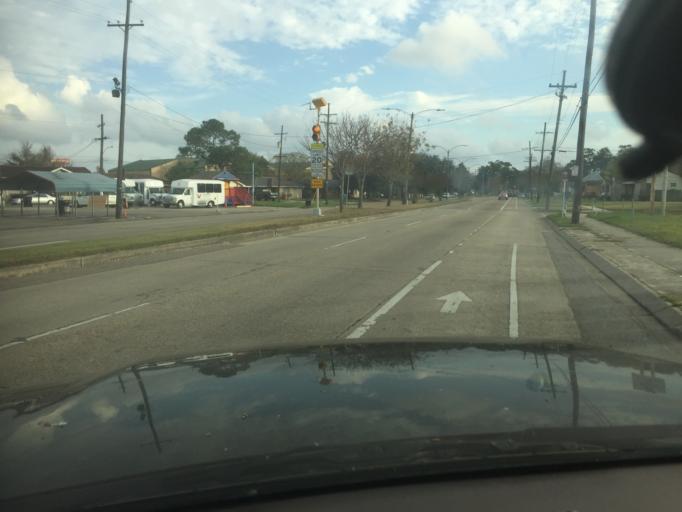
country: US
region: Louisiana
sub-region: Orleans Parish
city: New Orleans
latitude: 29.9910
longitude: -90.0763
